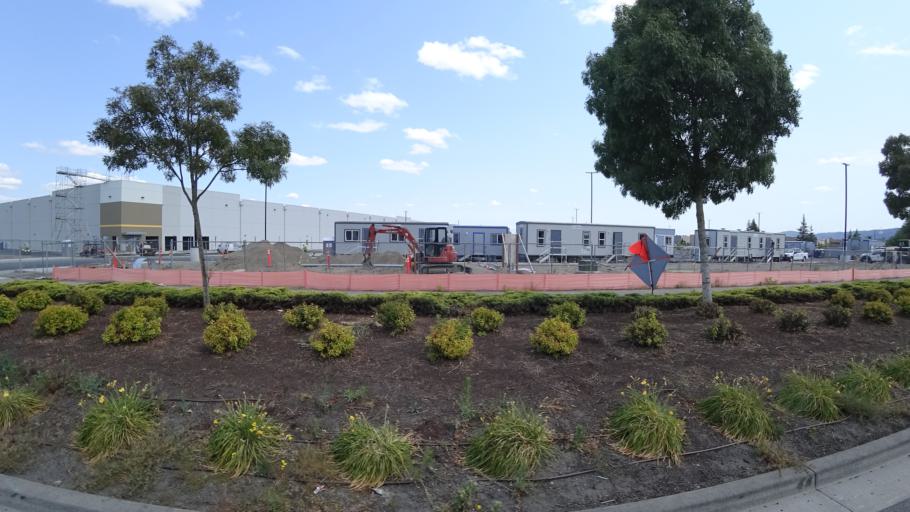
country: US
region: Washington
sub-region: Clark County
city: Lake Shore
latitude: 45.6337
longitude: -122.7716
